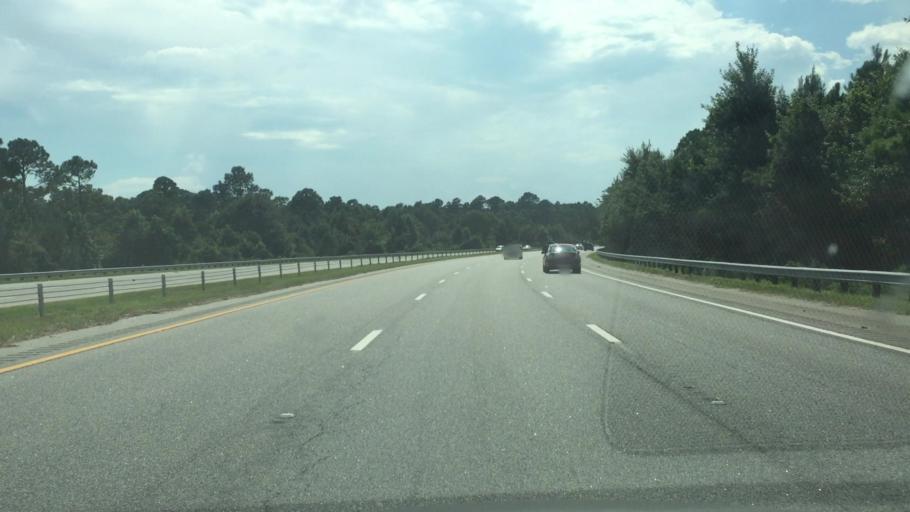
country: US
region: South Carolina
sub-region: Horry County
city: North Myrtle Beach
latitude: 33.8267
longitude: -78.7251
